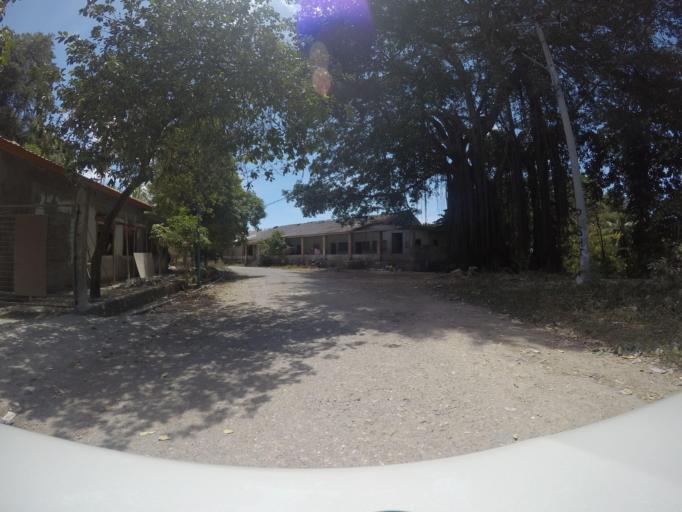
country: TL
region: Baucau
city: Baucau
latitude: -8.4595
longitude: 126.4507
